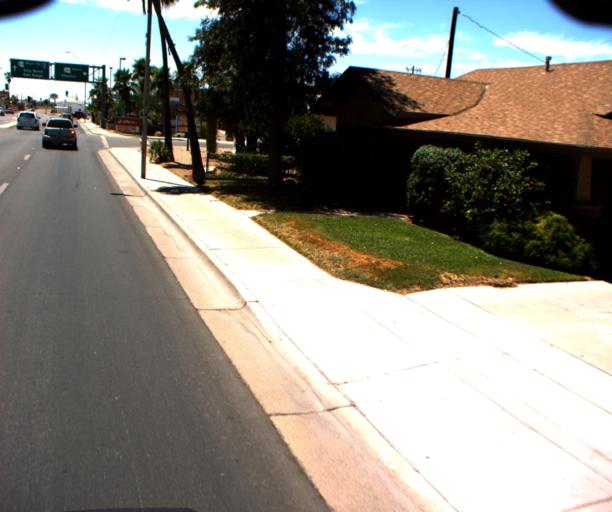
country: US
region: Arizona
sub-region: Pinal County
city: Casa Grande
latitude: 32.8796
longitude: -111.7555
